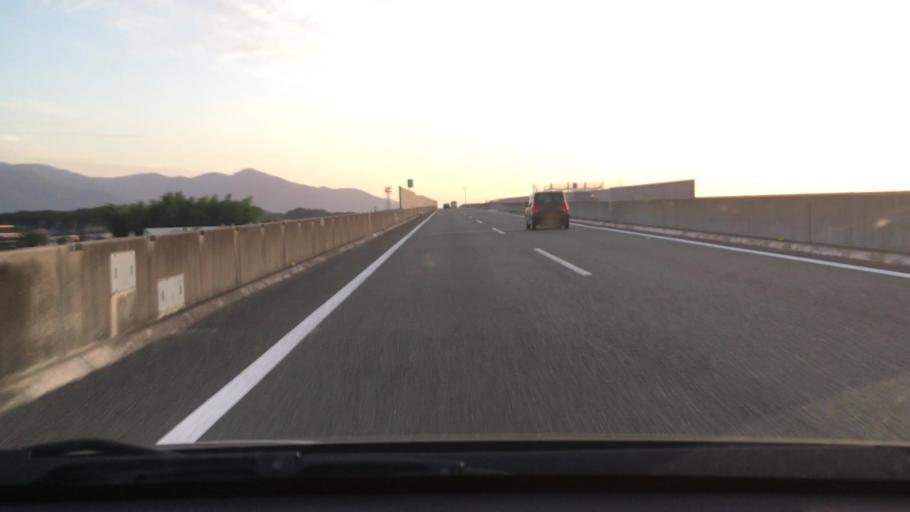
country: JP
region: Fukuoka
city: Maebaru-chuo
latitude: 33.5504
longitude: 130.2176
